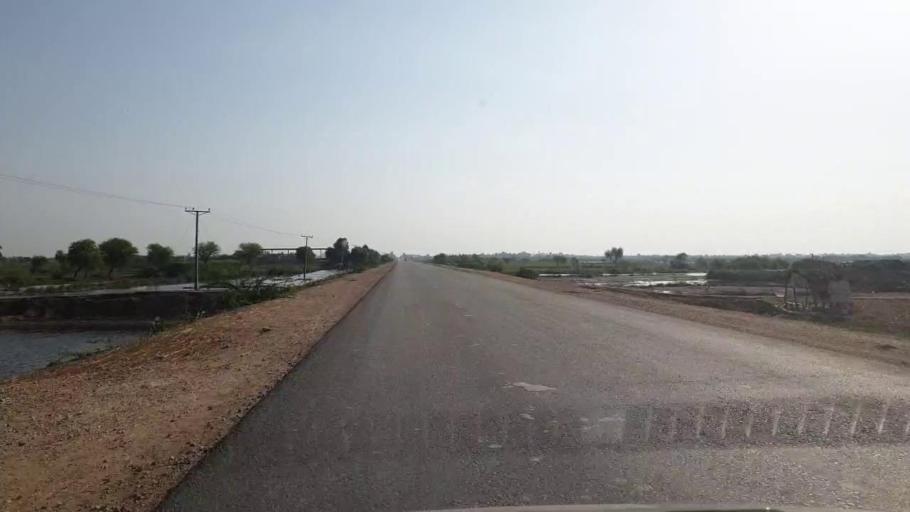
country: PK
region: Sindh
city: Badin
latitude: 24.6583
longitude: 68.9563
